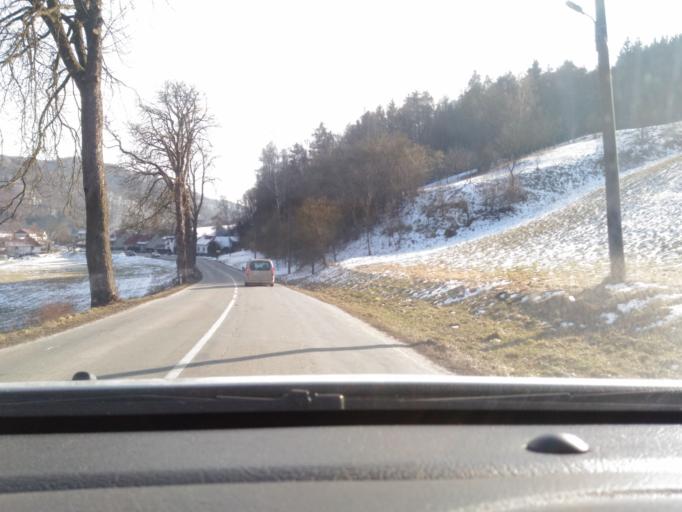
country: CZ
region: South Moravian
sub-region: Okres Brno-Venkov
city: Nedvedice
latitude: 49.4497
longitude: 16.3419
